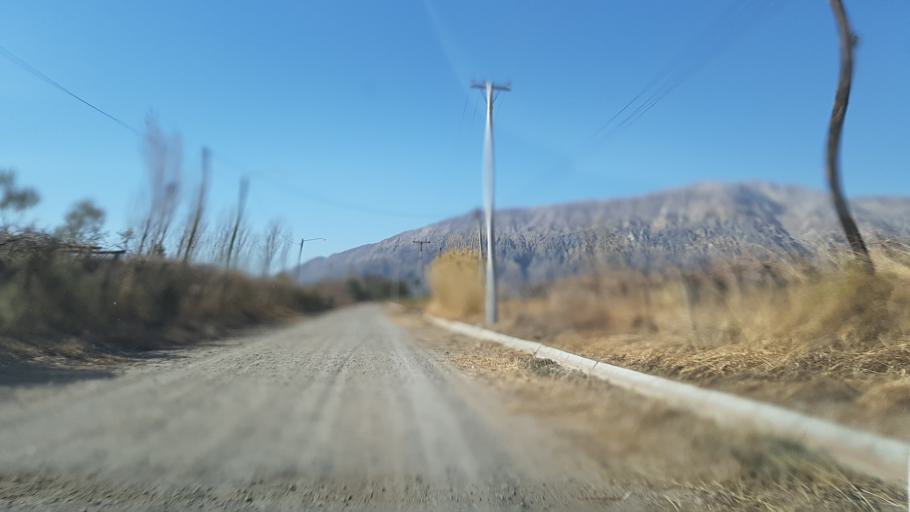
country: AR
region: San Juan
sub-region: Departamento de Zonda
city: Zonda
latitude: -31.5711
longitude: -68.7497
